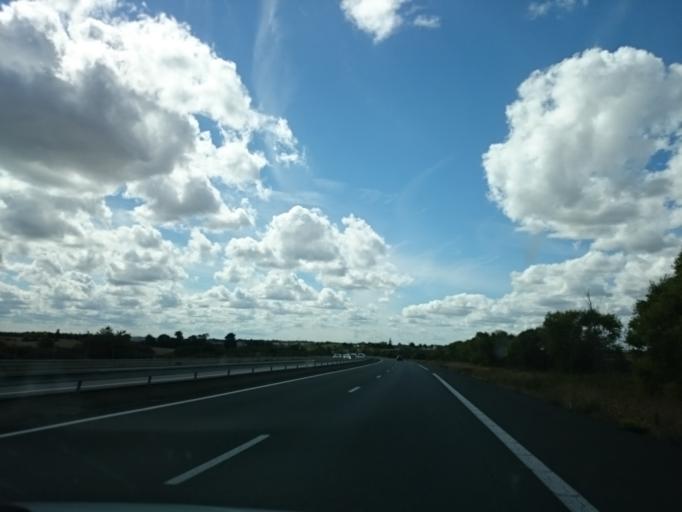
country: FR
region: Pays de la Loire
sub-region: Departement de Maine-et-Loire
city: Ingrandes
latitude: 47.4281
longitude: -0.9255
